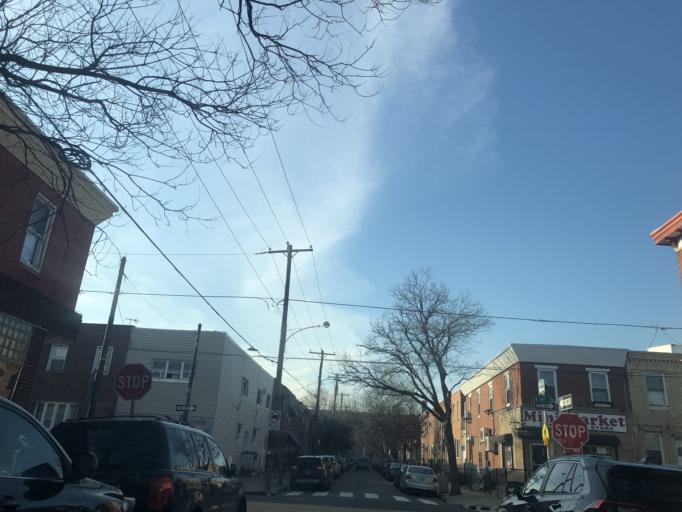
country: US
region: Pennsylvania
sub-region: Philadelphia County
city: Philadelphia
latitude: 39.9269
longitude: -75.1602
